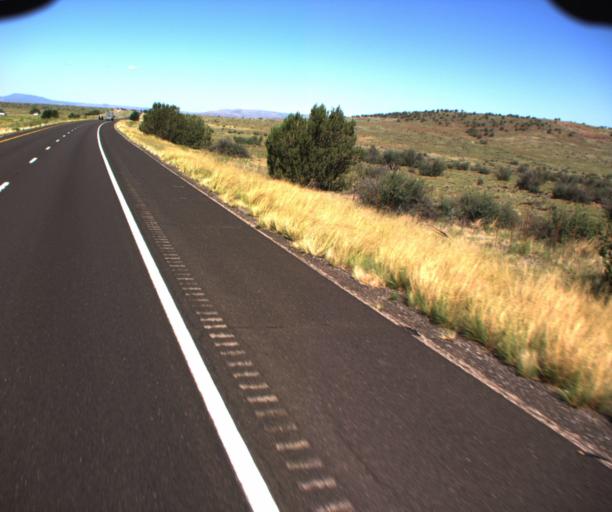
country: US
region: Arizona
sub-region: Yavapai County
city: Paulden
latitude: 35.2737
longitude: -112.7599
